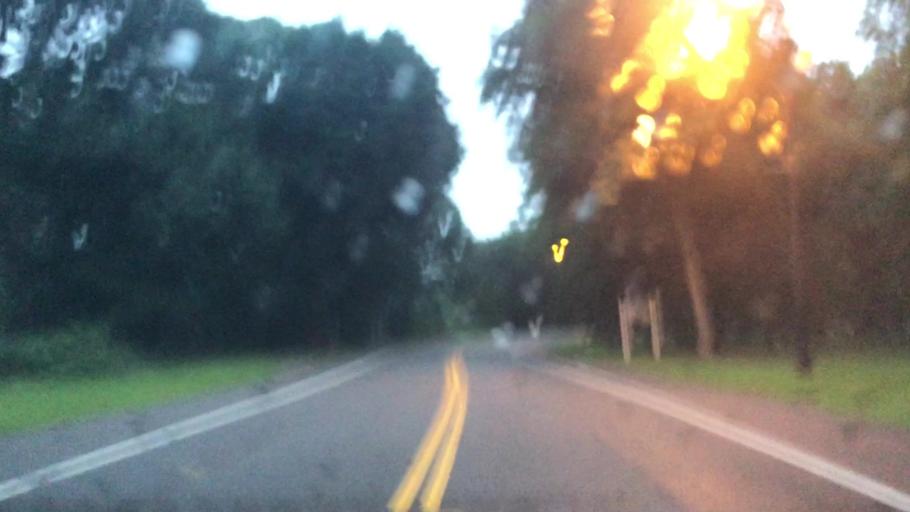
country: US
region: New York
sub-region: Nassau County
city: Lakeview
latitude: 40.6774
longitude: -73.6470
